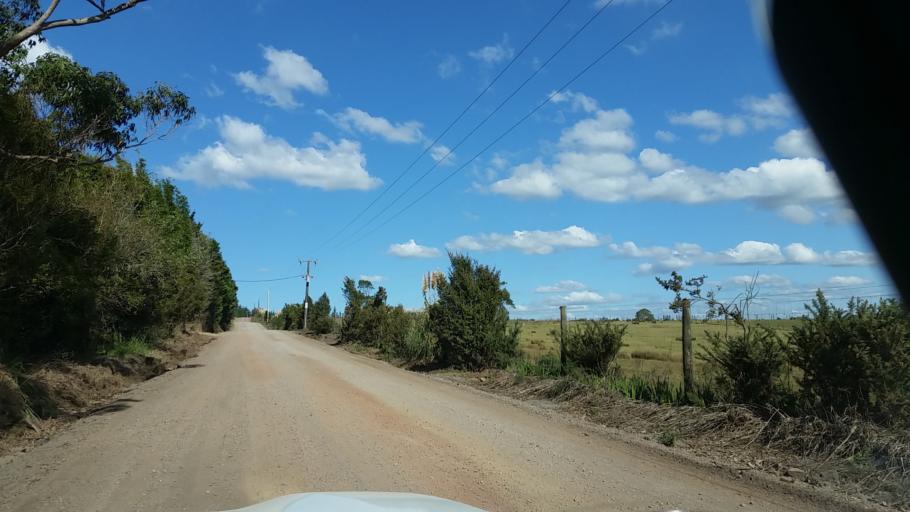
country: NZ
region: Northland
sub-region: Whangarei
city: Whangarei
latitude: -35.5808
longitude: 174.3105
